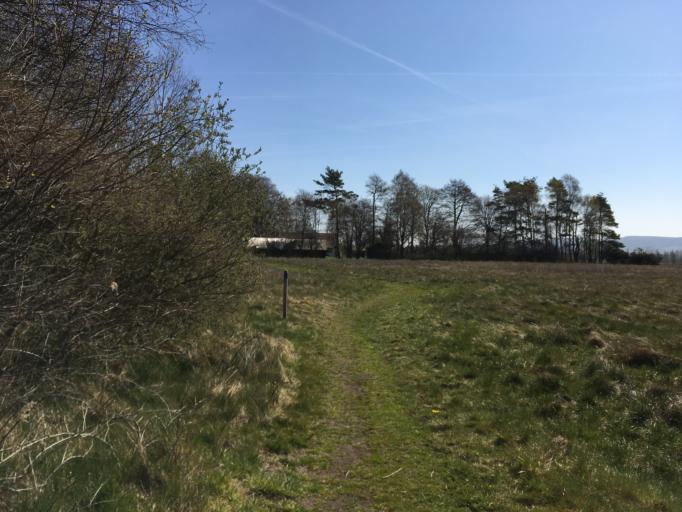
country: SE
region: Skane
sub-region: Bastads Kommun
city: Bastad
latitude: 56.4457
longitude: 12.9120
